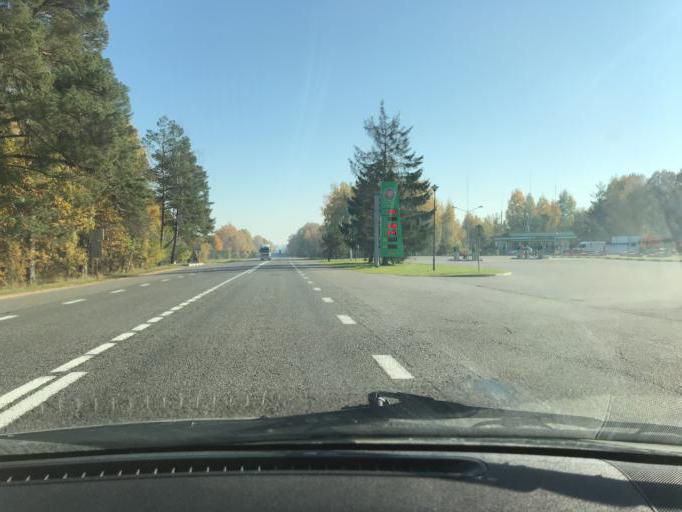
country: BY
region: Brest
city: Lyakhavichy
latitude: 52.9562
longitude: 26.3030
